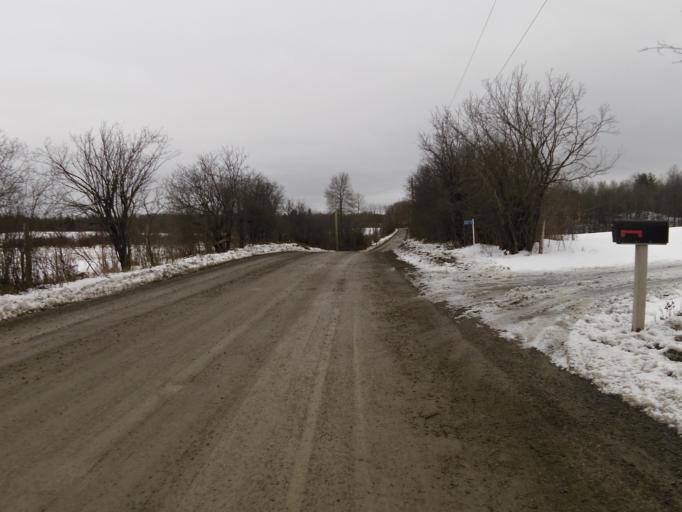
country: CA
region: Ontario
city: Carleton Place
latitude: 45.1976
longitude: -76.2146
